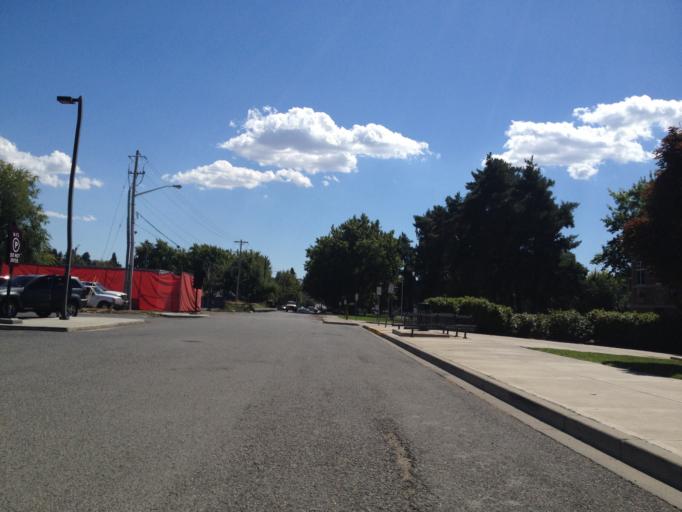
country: US
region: Washington
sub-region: Kittitas County
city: Ellensburg
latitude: 47.0022
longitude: -120.5376
